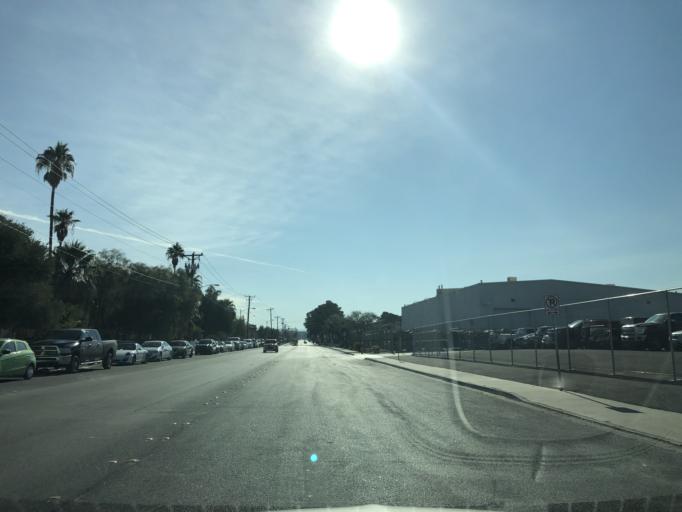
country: US
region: Nevada
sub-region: Clark County
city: Winchester
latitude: 36.1293
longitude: -115.1415
